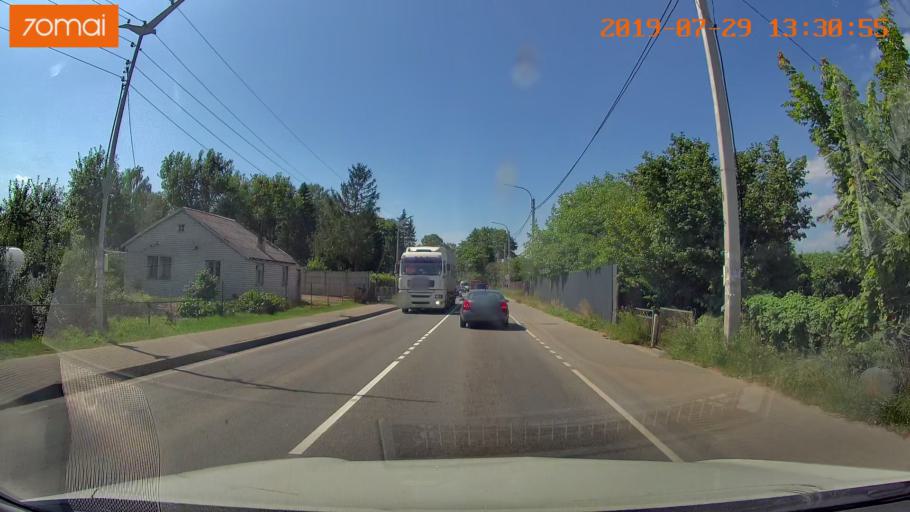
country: RU
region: Kaliningrad
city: Vzmorye
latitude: 54.6982
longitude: 20.2514
